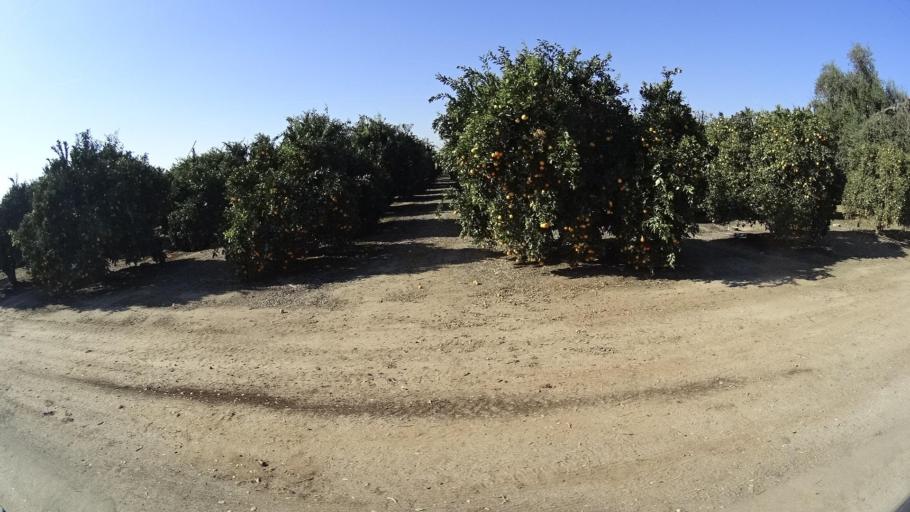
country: US
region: California
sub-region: Tulare County
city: Richgrove
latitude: 35.7285
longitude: -119.1429
